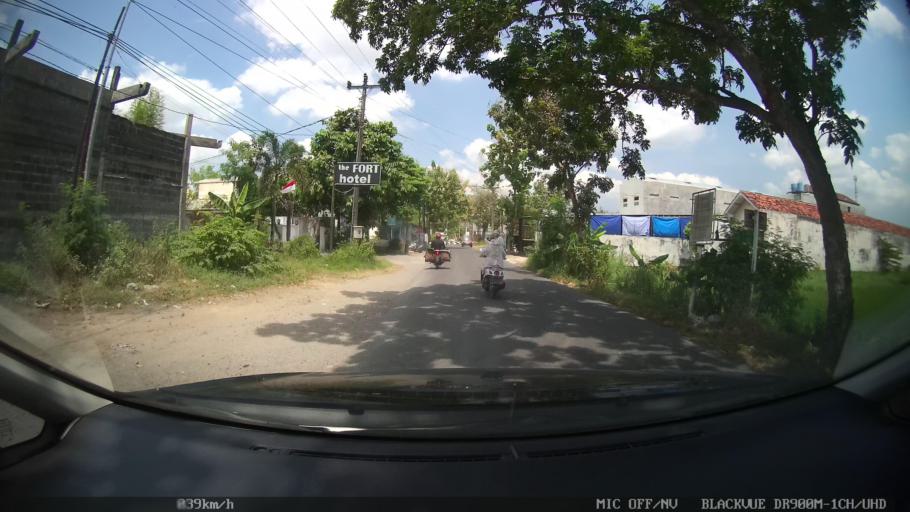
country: ID
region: Daerah Istimewa Yogyakarta
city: Kasihan
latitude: -7.8259
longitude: 110.3470
